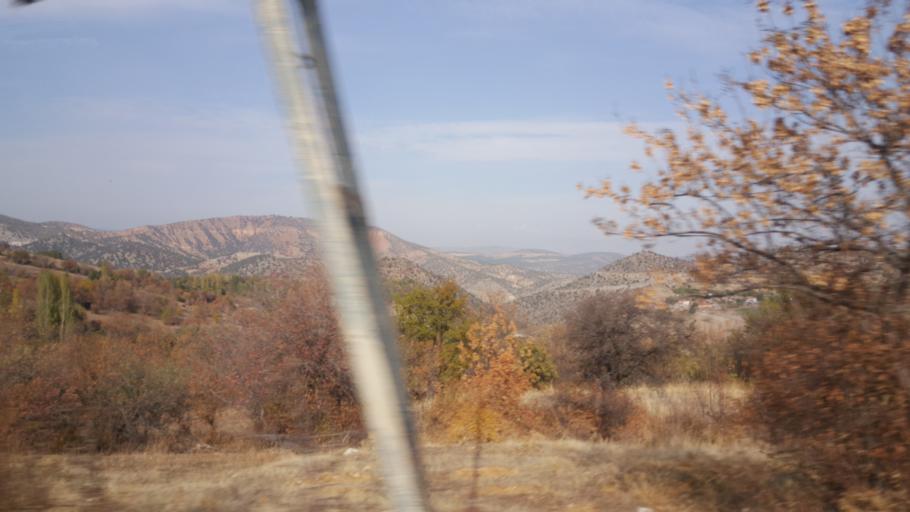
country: TR
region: Eskisehir
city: Mihaliccik
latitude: 39.9830
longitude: 31.3607
